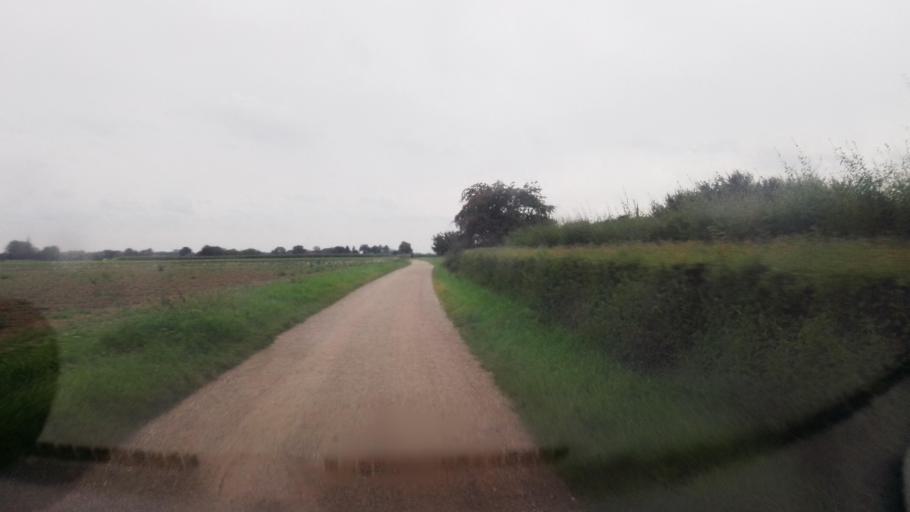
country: NL
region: Limburg
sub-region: Gemeente Venlo
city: Venlo
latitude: 51.4254
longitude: 6.1523
